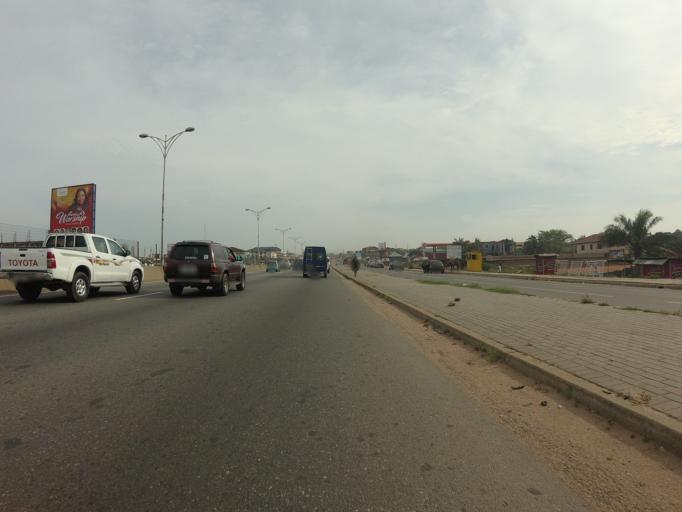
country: GH
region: Greater Accra
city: Gbawe
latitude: 5.5949
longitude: -0.2660
